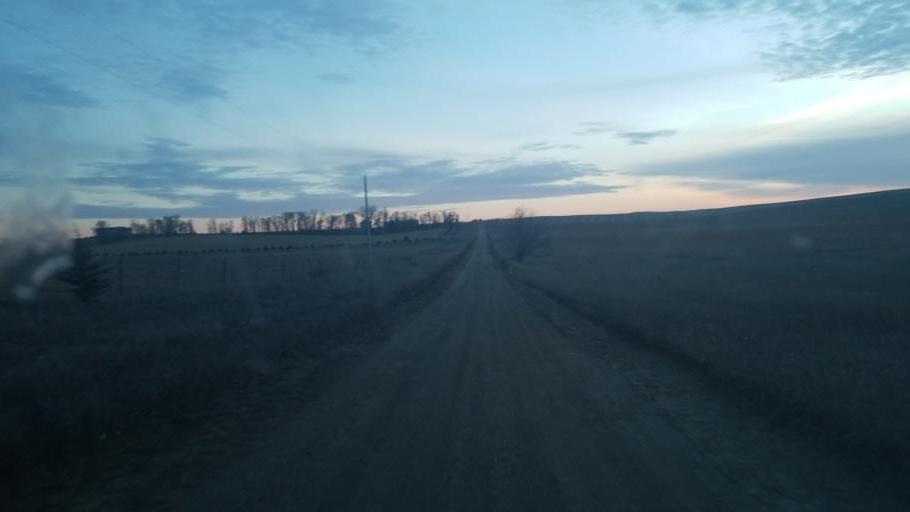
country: US
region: Nebraska
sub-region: Knox County
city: Center
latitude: 42.6539
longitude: -97.7991
